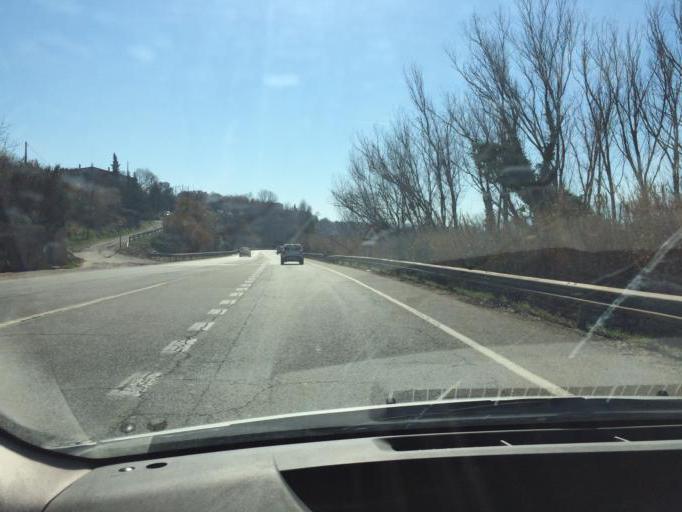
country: ES
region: Catalonia
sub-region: Provincia de Barcelona
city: Sant Joan de Vilatorrada
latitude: 41.7358
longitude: 1.8112
